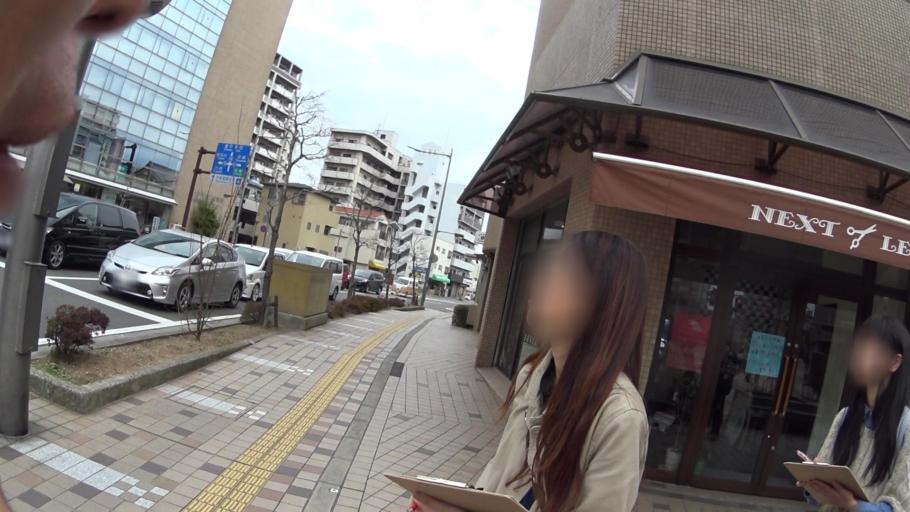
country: JP
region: Hyogo
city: Itami
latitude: 34.7832
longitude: 135.4159
